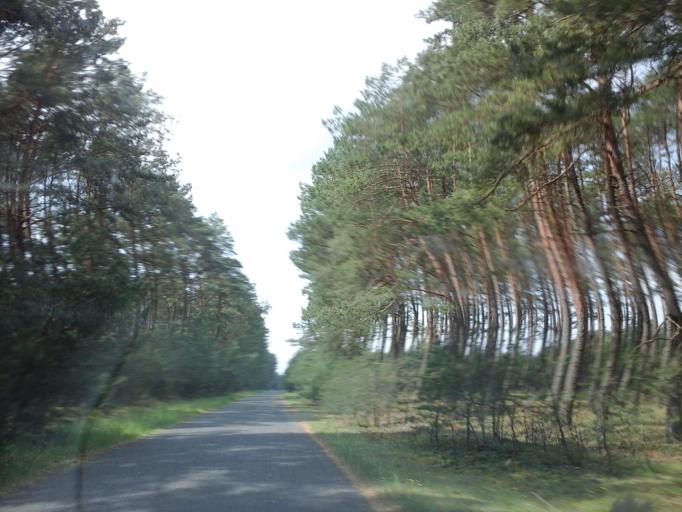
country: PL
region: West Pomeranian Voivodeship
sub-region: Powiat drawski
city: Kalisz Pomorski
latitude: 53.1991
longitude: 15.9097
